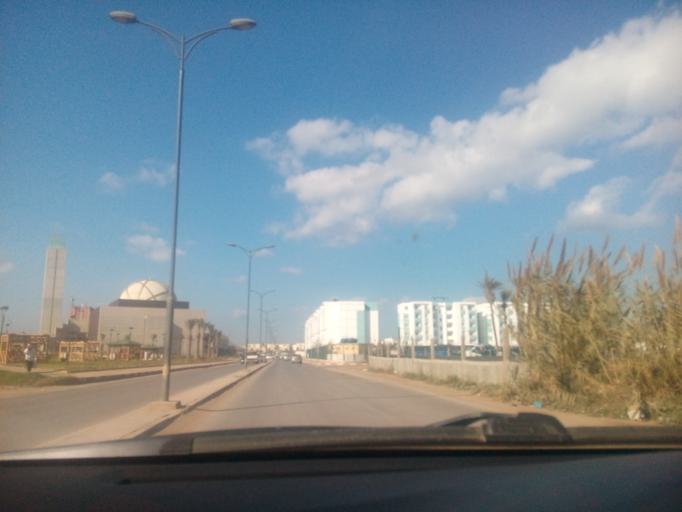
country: DZ
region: Oran
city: Es Senia
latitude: 35.6782
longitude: -0.5989
